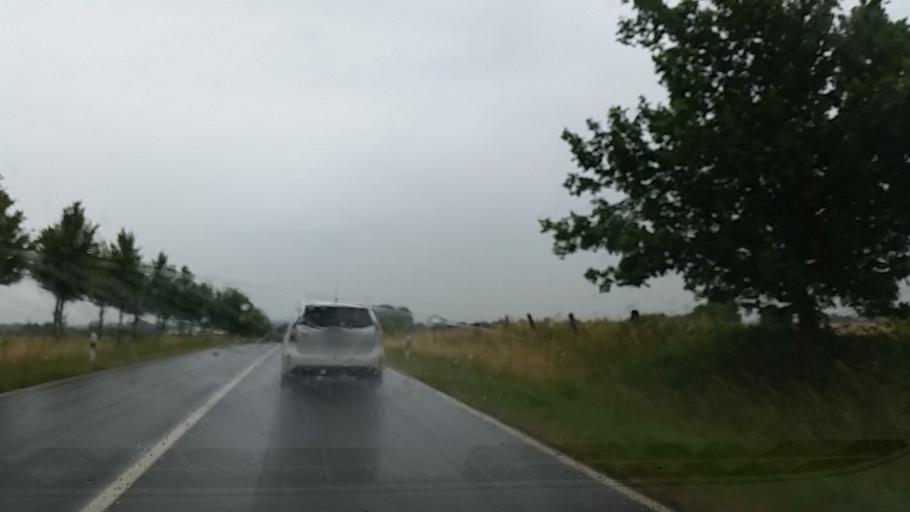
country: DE
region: Mecklenburg-Vorpommern
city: Kropelin
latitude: 54.0804
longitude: 11.8369
